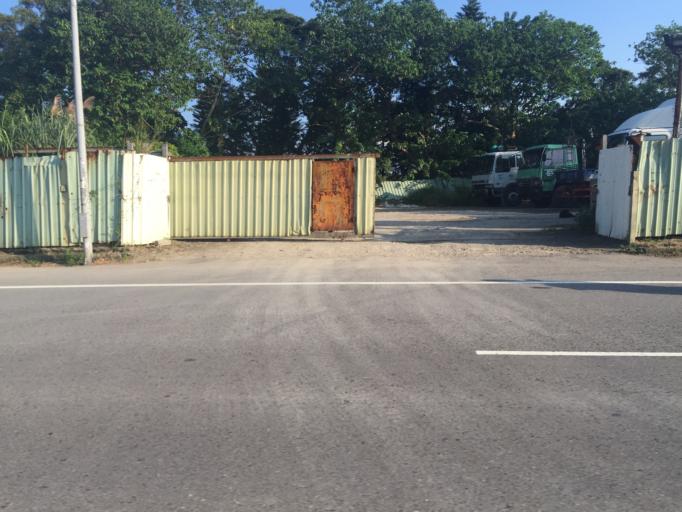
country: TW
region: Taiwan
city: Daxi
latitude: 24.9219
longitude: 121.2561
